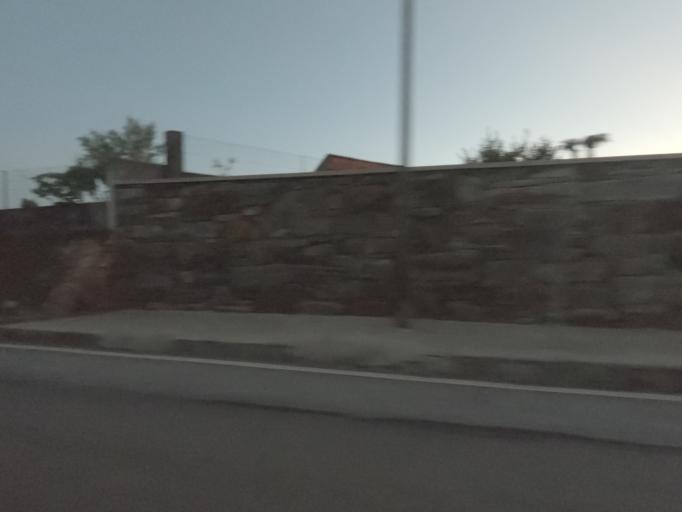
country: PT
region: Vila Real
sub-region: Sabrosa
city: Vilela
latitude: 41.2371
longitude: -7.6829
